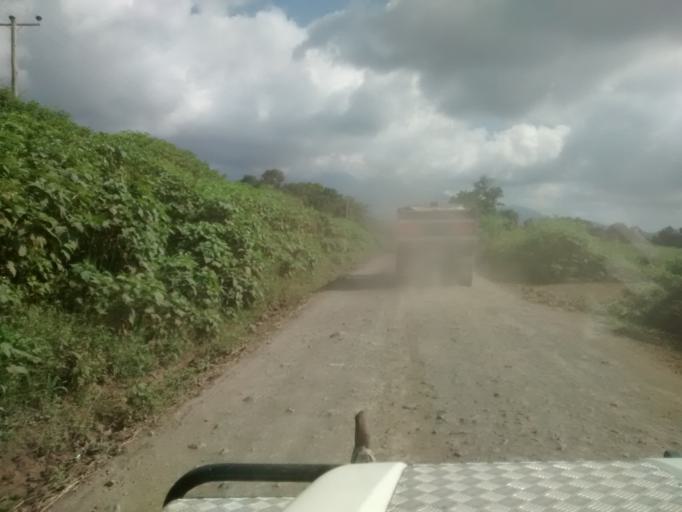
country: TZ
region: Arusha
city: Usa River
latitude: -3.3652
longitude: 36.8449
